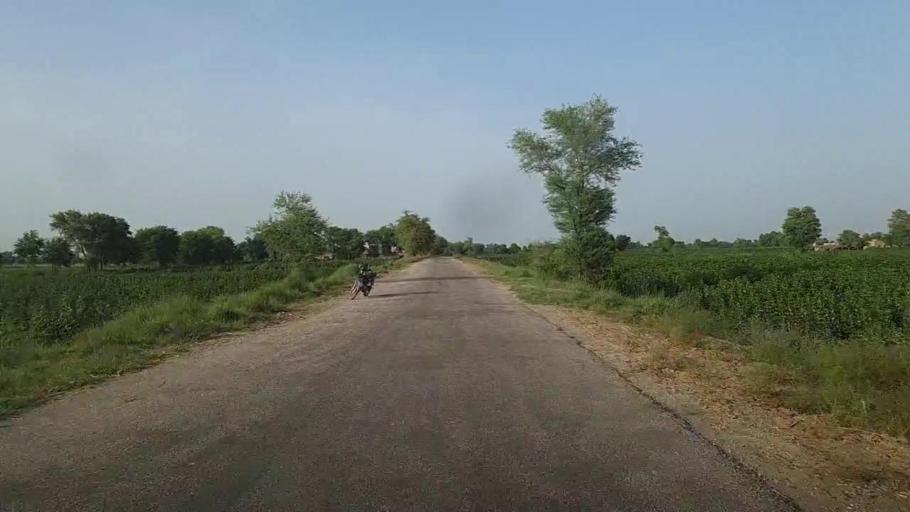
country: PK
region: Sindh
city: Ubauro
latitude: 28.1128
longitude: 69.8201
